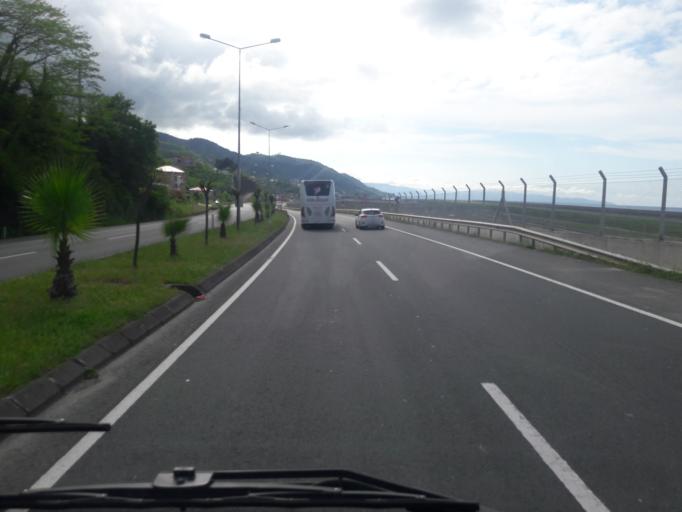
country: TR
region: Giresun
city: Piraziz
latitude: 40.9627
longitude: 38.0954
